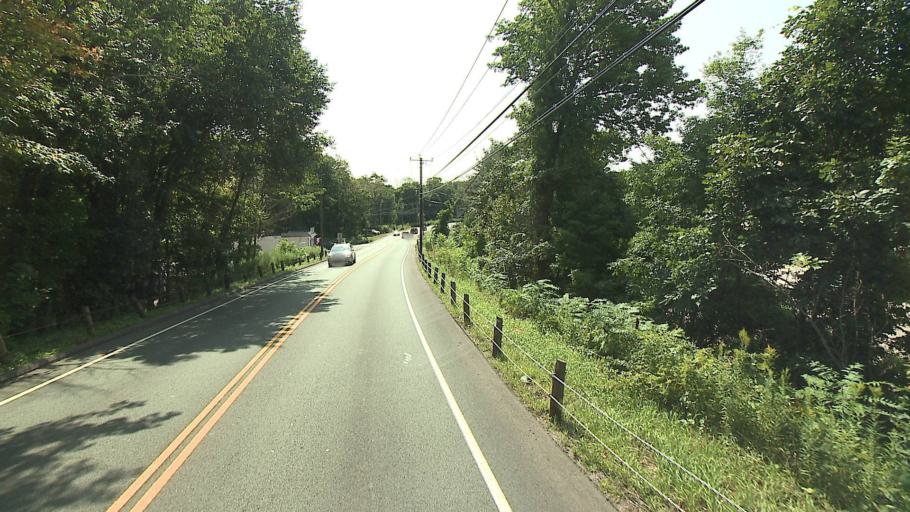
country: US
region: Connecticut
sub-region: Fairfield County
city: Newtown
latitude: 41.3558
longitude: -73.2621
